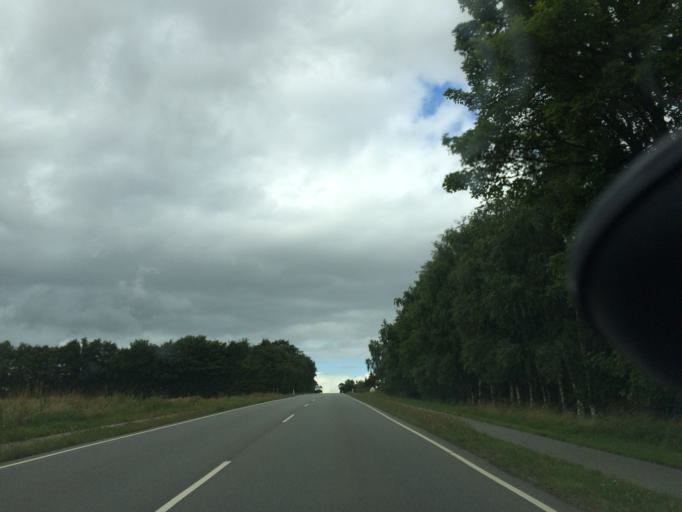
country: DK
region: Central Jutland
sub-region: Skanderborg Kommune
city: Galten
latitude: 56.1484
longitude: 9.8839
